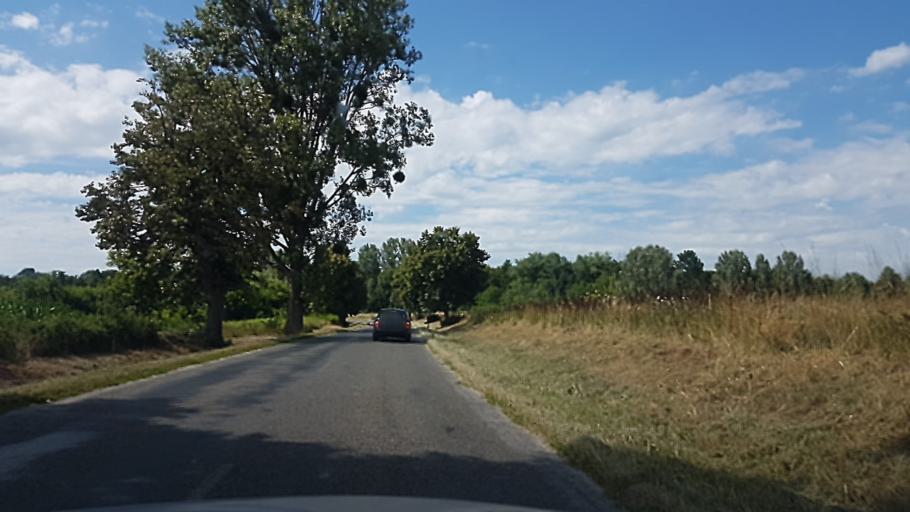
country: HU
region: Somogy
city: Barcs
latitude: 45.9587
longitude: 17.5966
